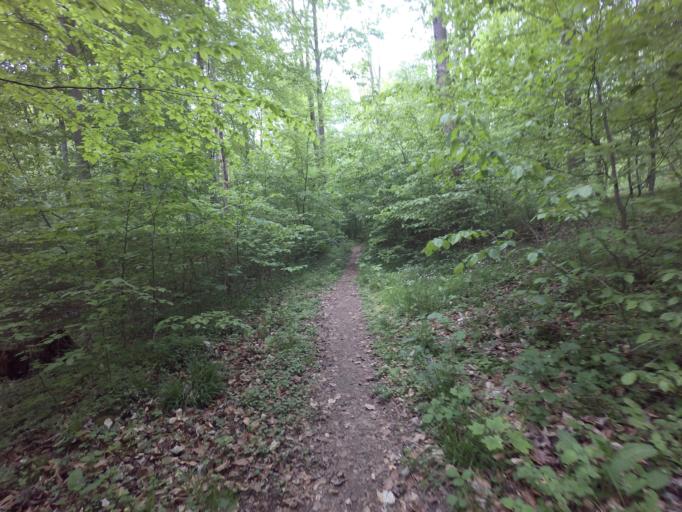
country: DE
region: Lower Saxony
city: Diekholzen
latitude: 52.1145
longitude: 9.9082
